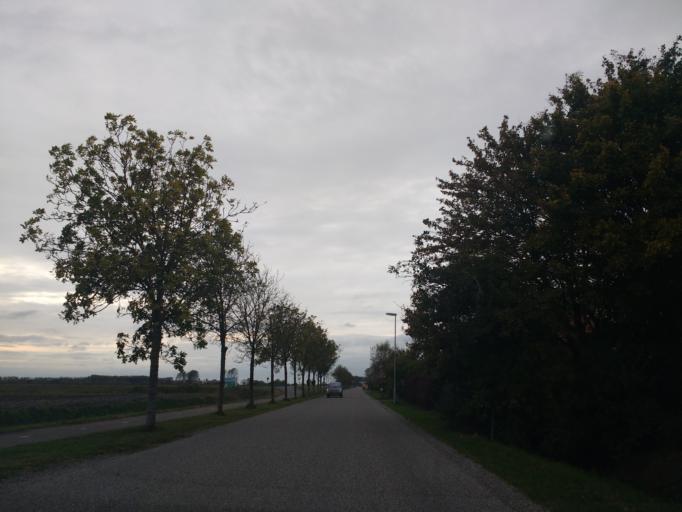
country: NL
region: Zeeland
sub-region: Gemeente Vlissingen
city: Vlissingen
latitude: 51.3965
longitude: 3.5401
